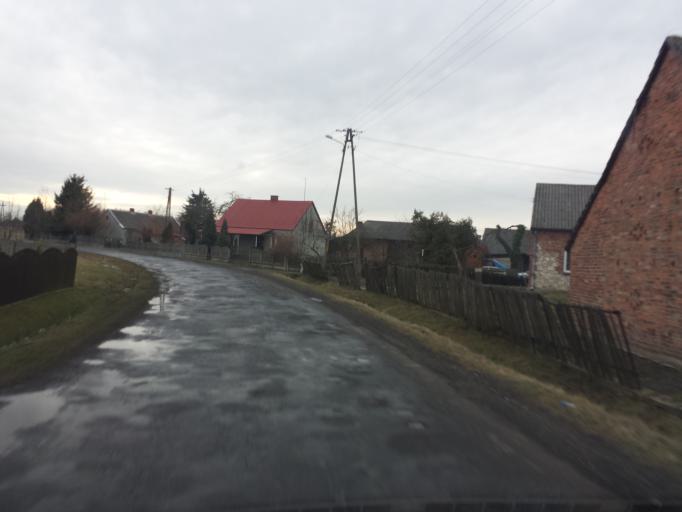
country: PL
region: Lodz Voivodeship
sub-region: Powiat wielunski
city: Osjakow
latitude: 51.2991
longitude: 18.7413
